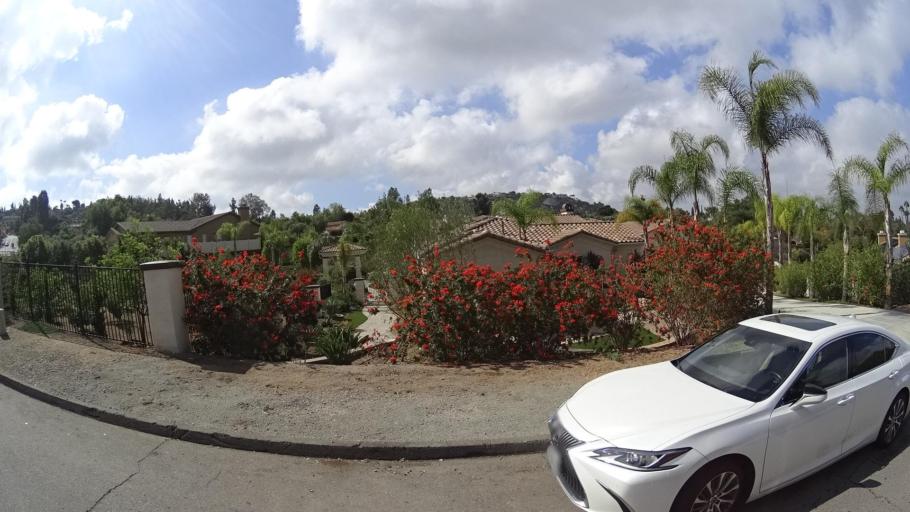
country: US
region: California
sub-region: San Diego County
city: Granite Hills
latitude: 32.7815
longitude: -116.9028
